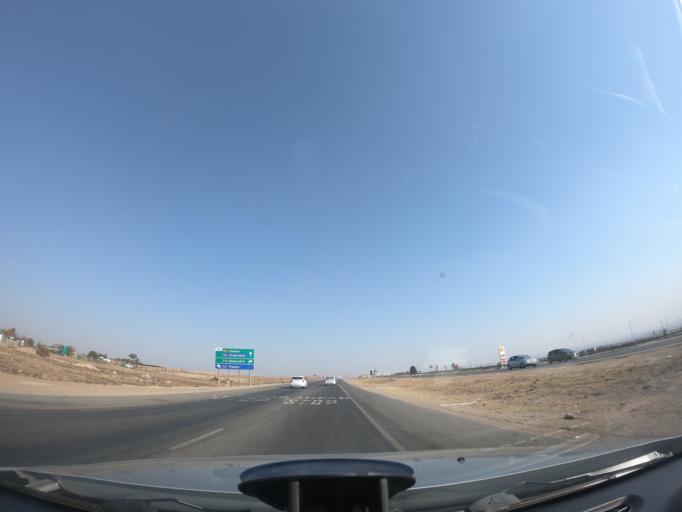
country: ZA
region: Gauteng
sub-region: City of Johannesburg Metropolitan Municipality
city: Diepsloot
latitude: -25.9066
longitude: 28.0271
